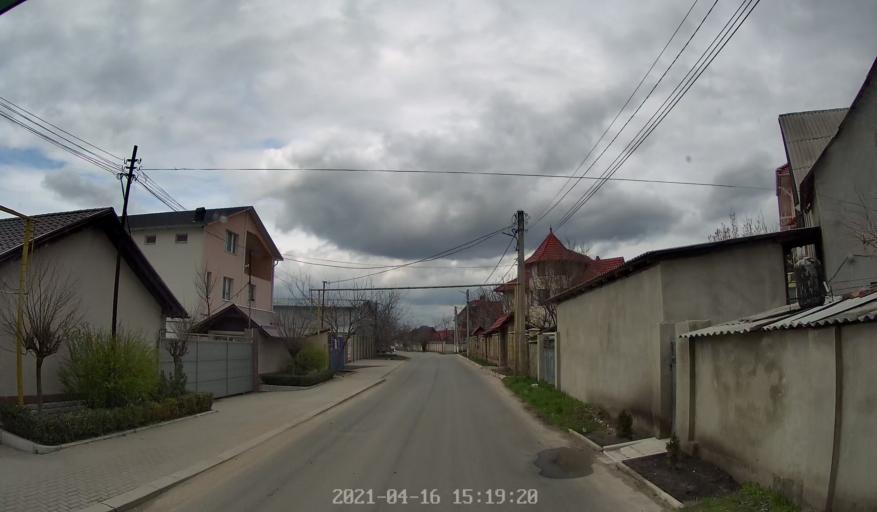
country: MD
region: Chisinau
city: Stauceni
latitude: 47.1033
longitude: 28.8647
